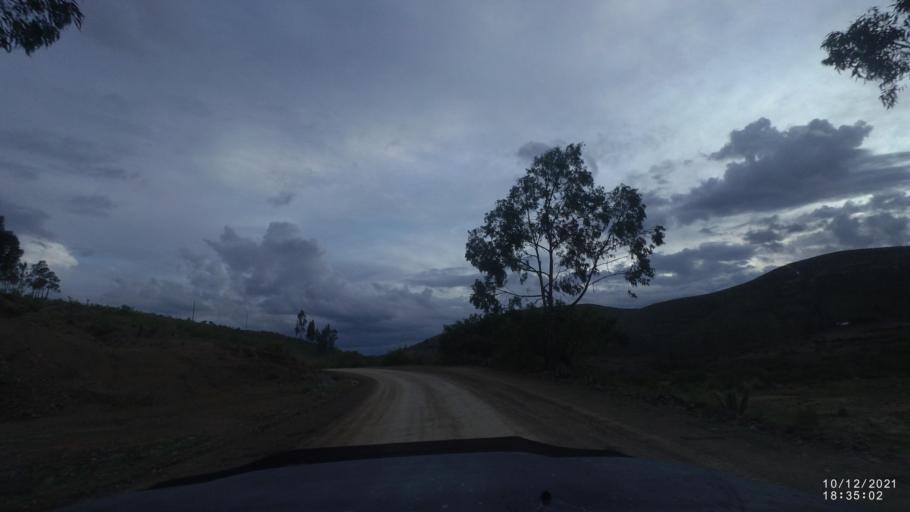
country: BO
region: Cochabamba
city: Tarata
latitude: -17.8253
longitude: -65.9904
